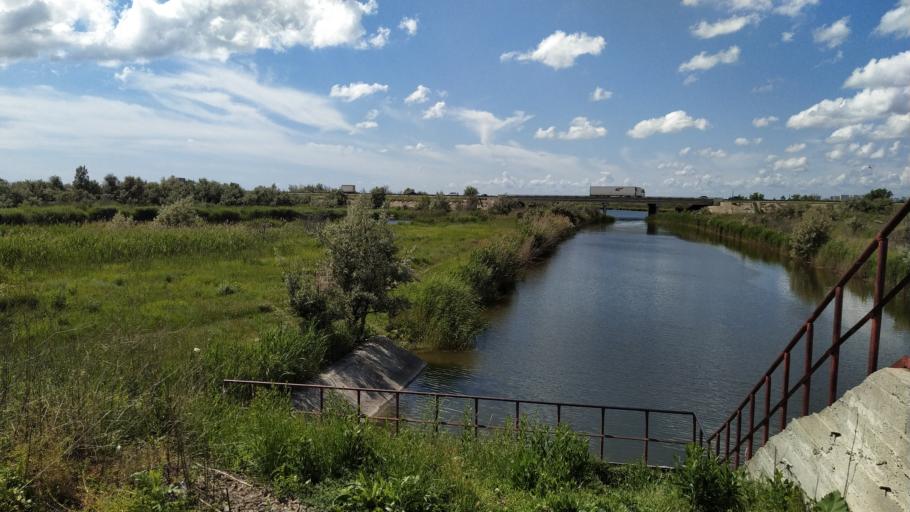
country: RU
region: Rostov
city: Bataysk
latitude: 47.1327
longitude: 39.6785
